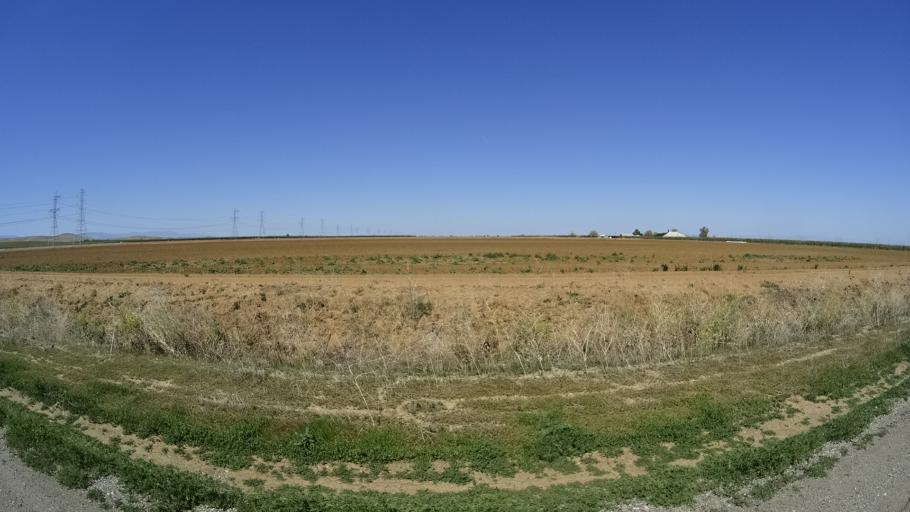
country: US
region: California
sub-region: Glenn County
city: Willows
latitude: 39.4802
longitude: -122.2825
